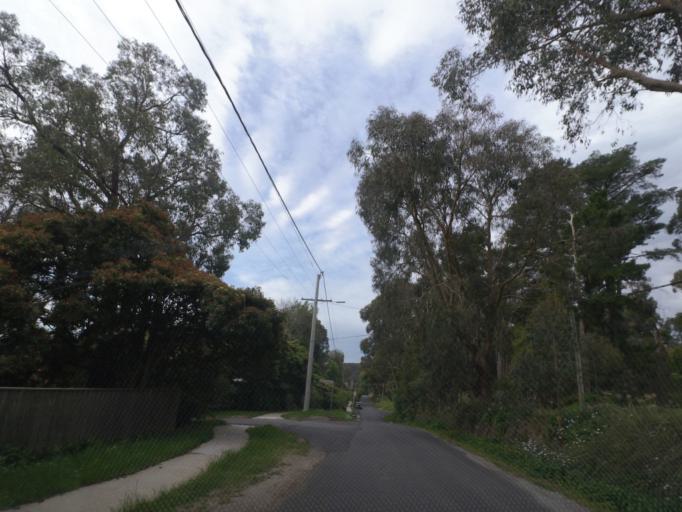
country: AU
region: Victoria
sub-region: Yarra Ranges
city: Montrose
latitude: -37.8116
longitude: 145.3561
